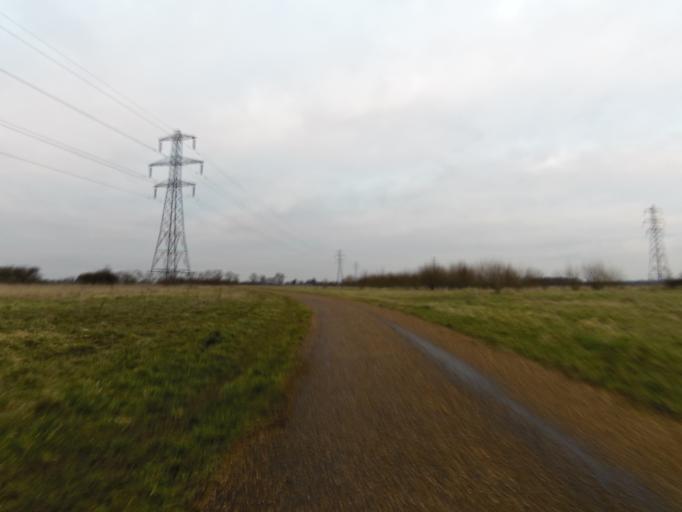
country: GB
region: England
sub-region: Cambridgeshire
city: Bottisham
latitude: 52.2609
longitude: 0.2470
